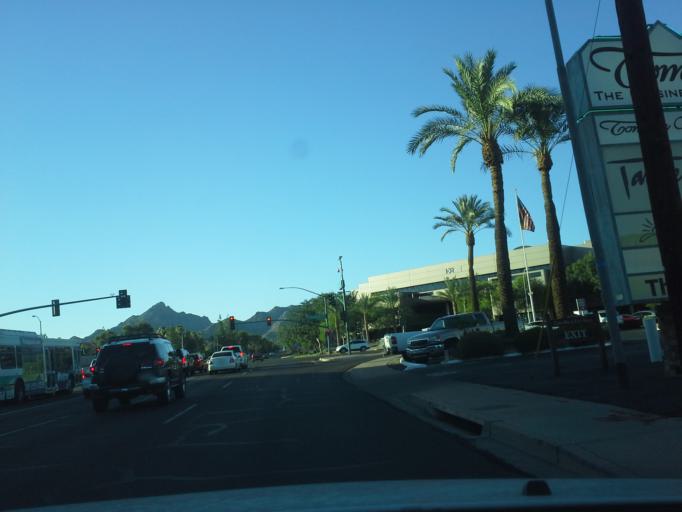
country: US
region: Arizona
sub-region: Maricopa County
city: Paradise Valley
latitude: 33.5093
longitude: -112.0129
